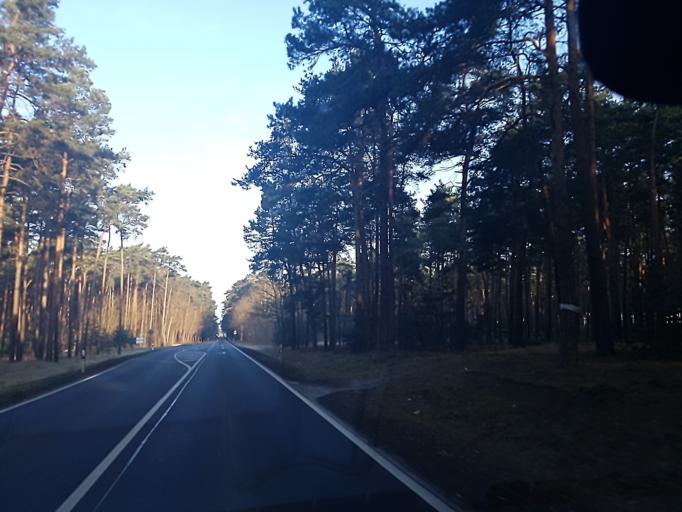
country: DE
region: Brandenburg
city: Linthe
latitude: 52.1621
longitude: 12.7770
